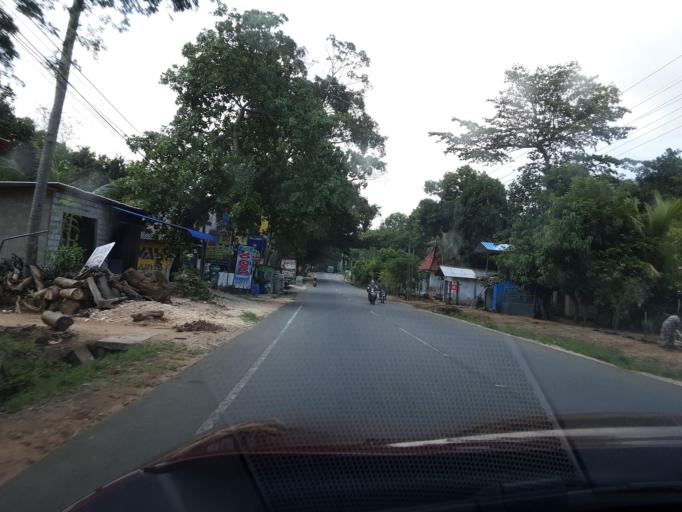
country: LK
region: Uva
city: Haputale
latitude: 6.6882
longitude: 81.1076
